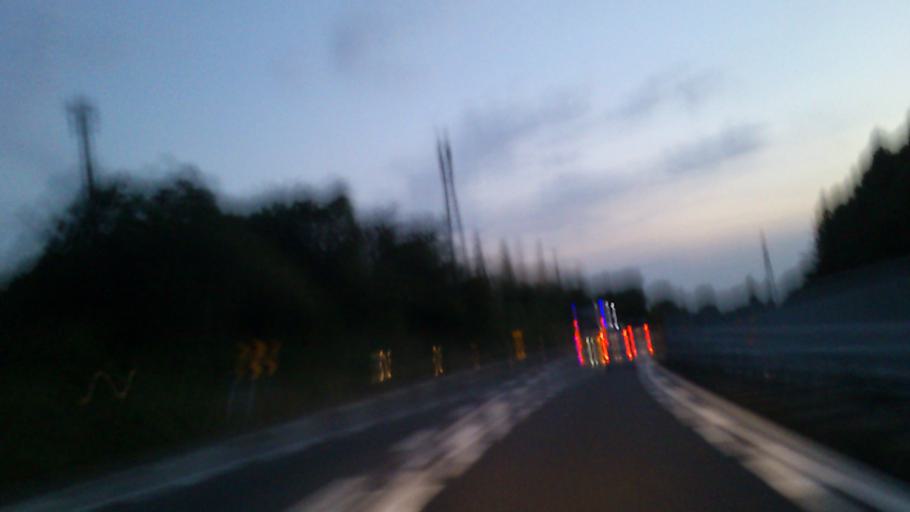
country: JP
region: Aichi
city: Kasugai
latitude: 35.3111
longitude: 137.0161
